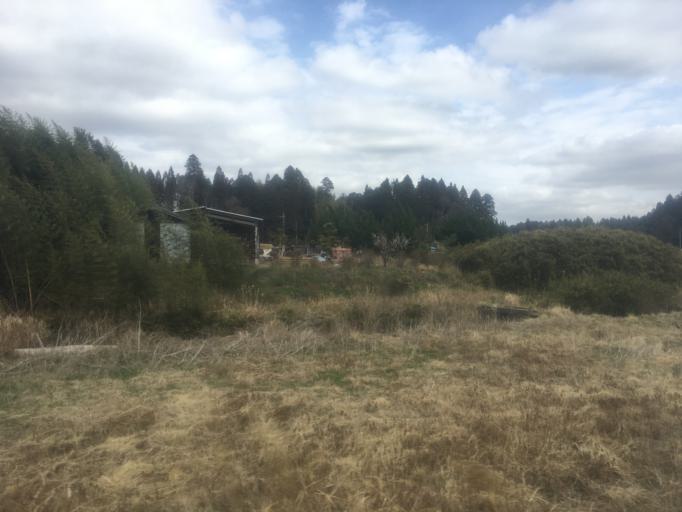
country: JP
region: Chiba
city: Yachimata
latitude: 35.6319
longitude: 140.3569
